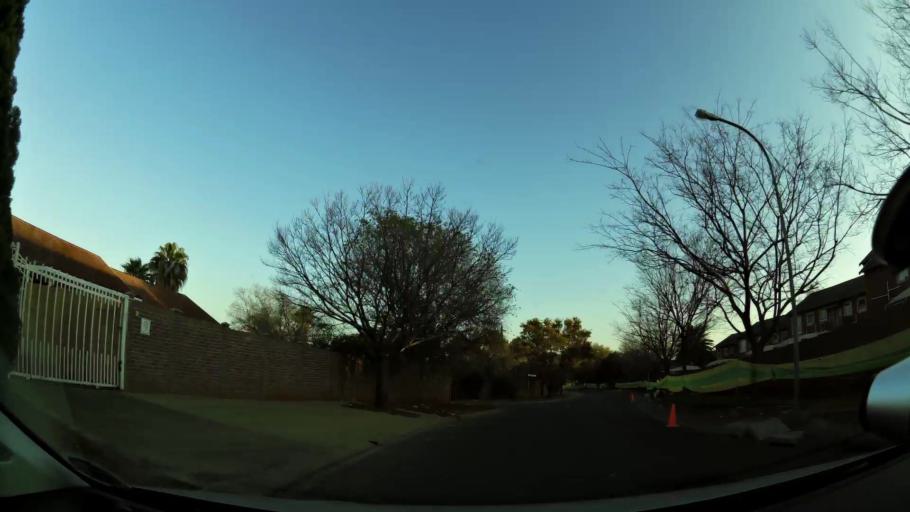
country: ZA
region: Orange Free State
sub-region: Mangaung Metropolitan Municipality
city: Bloemfontein
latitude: -29.0842
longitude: 26.1598
